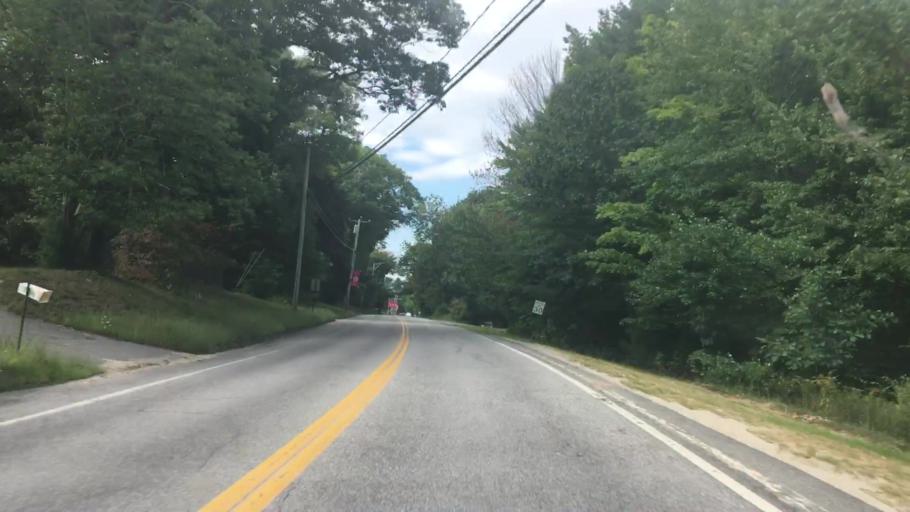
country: US
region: Maine
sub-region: Cumberland County
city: Raymond
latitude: 44.0007
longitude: -70.5197
